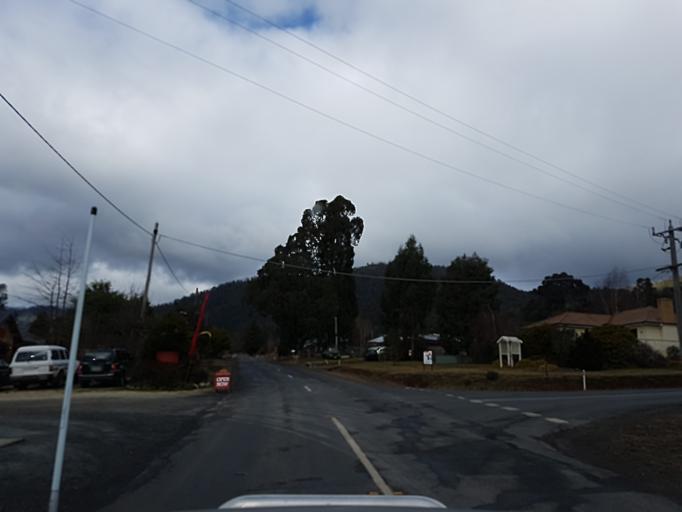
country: AU
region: Victoria
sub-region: Yarra Ranges
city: Millgrove
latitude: -37.5144
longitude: 145.7510
